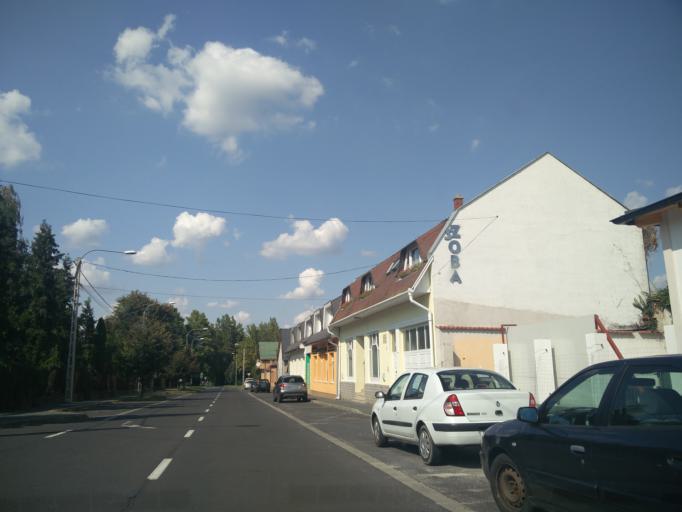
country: HU
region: Zala
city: Zalaegerszeg
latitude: 46.8468
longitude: 16.8353
